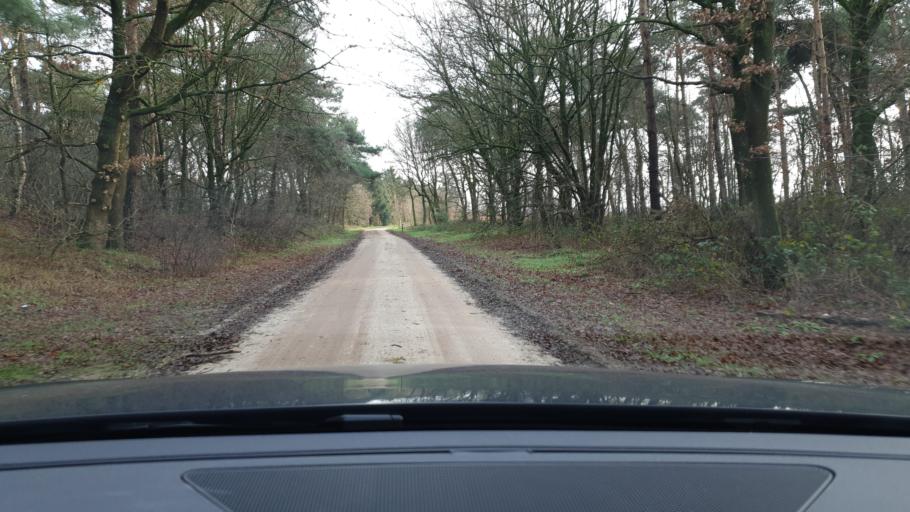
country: NL
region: Limburg
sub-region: Gemeente Peel en Maas
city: Maasbree
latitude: 51.4359
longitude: 6.0708
